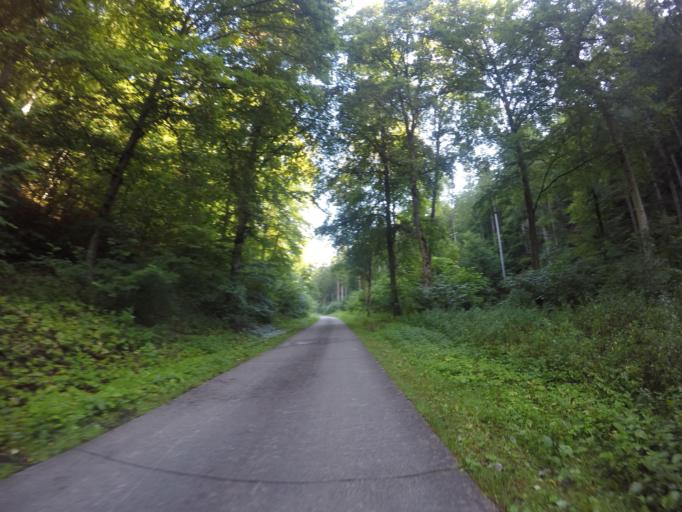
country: DE
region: Baden-Wuerttemberg
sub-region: Tuebingen Region
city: Schelklingen
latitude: 48.3856
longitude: 9.7330
